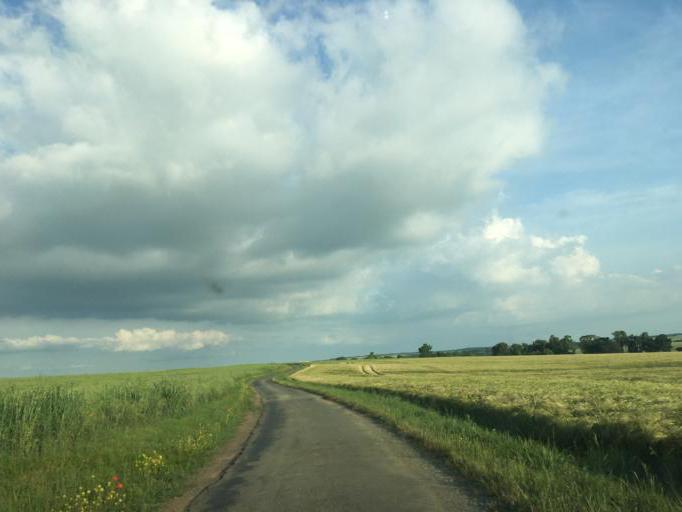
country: FR
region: Poitou-Charentes
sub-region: Departement des Deux-Sevres
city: Mauze-sur-le-Mignon
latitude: 46.0834
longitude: -0.5800
